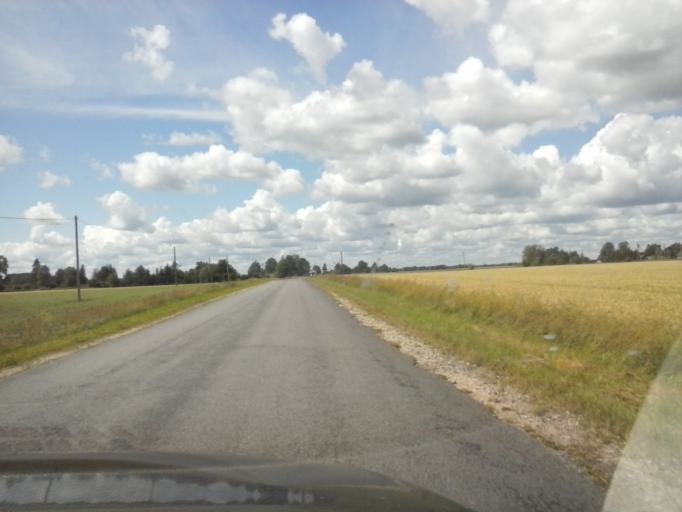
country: EE
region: Laeaene-Virumaa
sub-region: Rakke vald
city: Rakke
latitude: 59.0542
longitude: 26.3526
